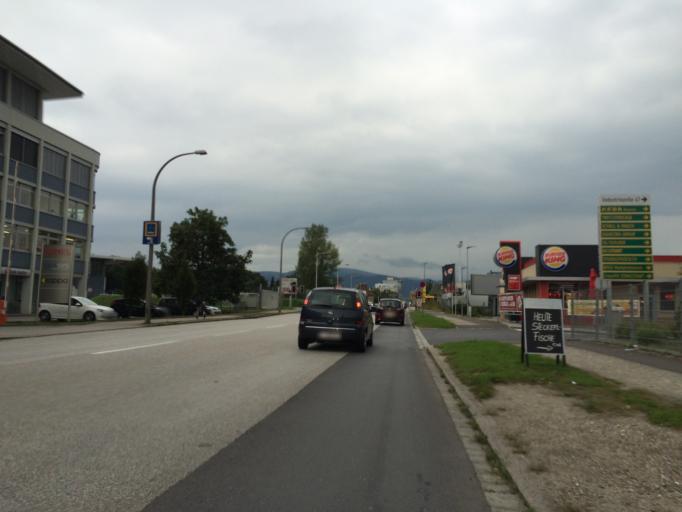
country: AT
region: Upper Austria
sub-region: Linz Stadt
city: Linz
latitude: 48.3079
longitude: 14.3157
